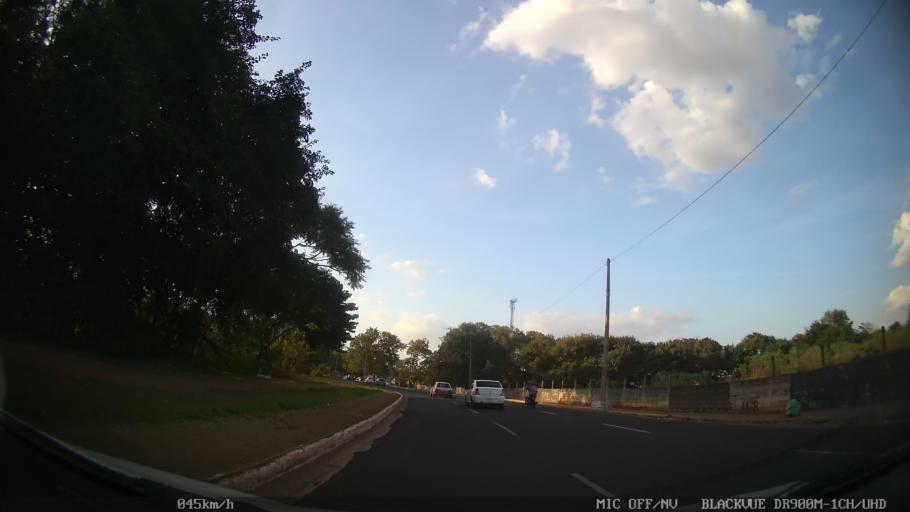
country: BR
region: Sao Paulo
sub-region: Ribeirao Preto
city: Ribeirao Preto
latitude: -21.1447
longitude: -47.8026
